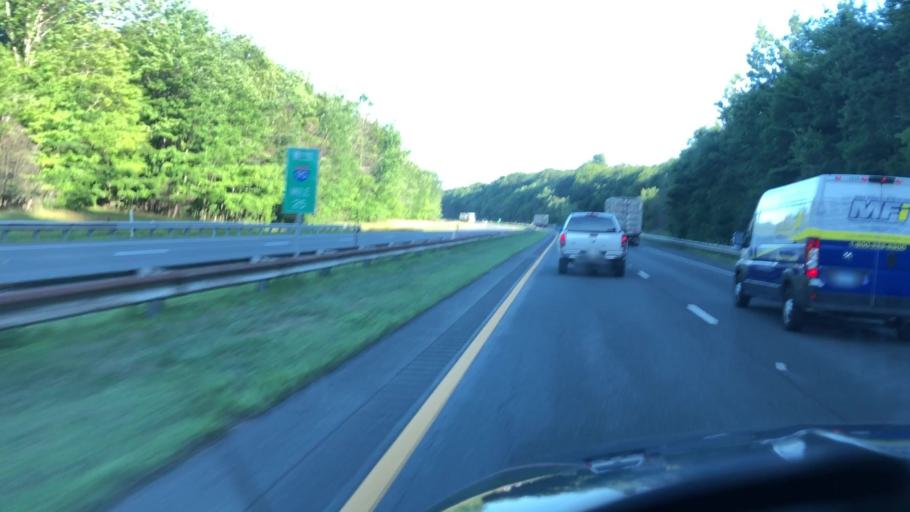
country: US
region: Massachusetts
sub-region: Berkshire County
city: Otis
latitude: 42.2353
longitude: -72.9905
